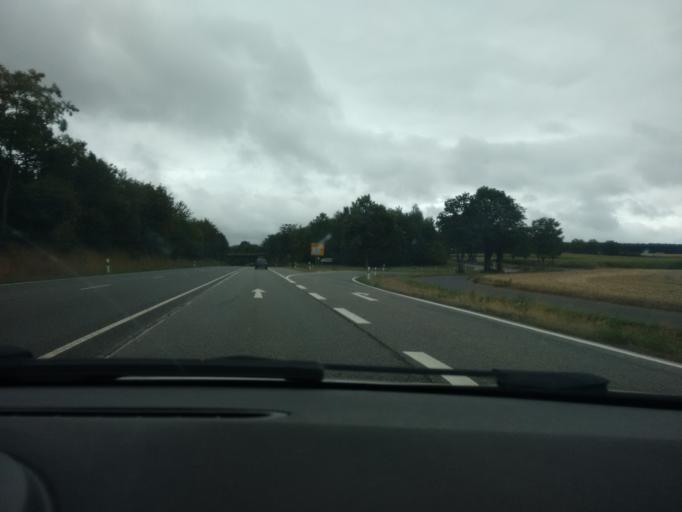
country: DE
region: Rheinland-Pfalz
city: Nussbaum
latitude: 49.7929
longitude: 7.6498
